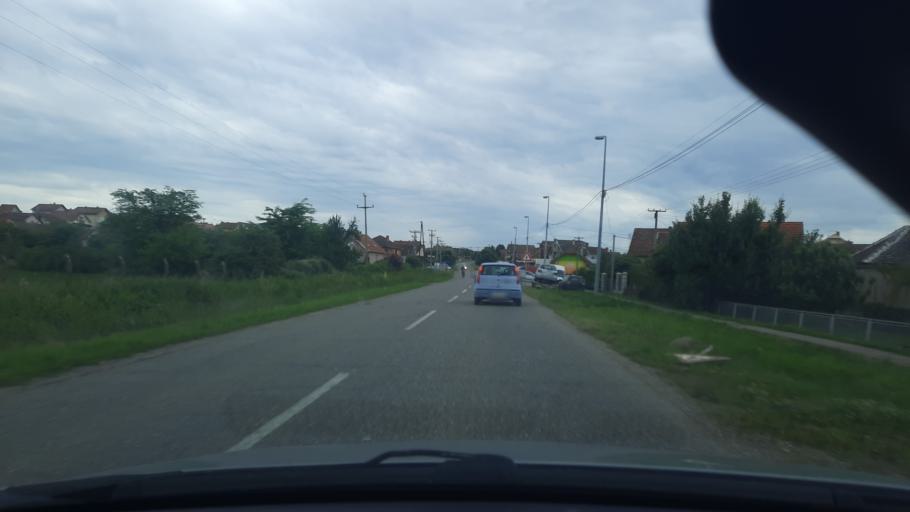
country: RS
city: Jevremovac
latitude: 44.7333
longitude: 19.6712
